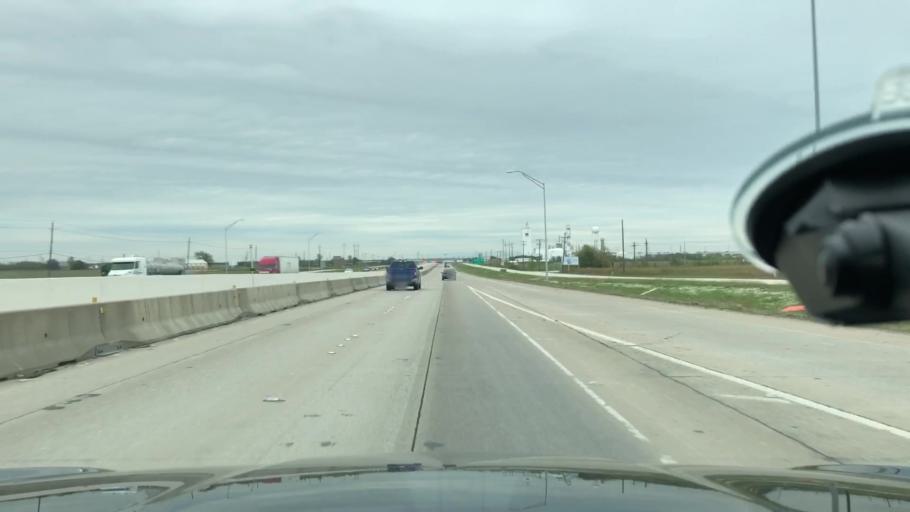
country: US
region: Texas
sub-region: Ellis County
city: Waxahachie
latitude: 32.4315
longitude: -96.8585
